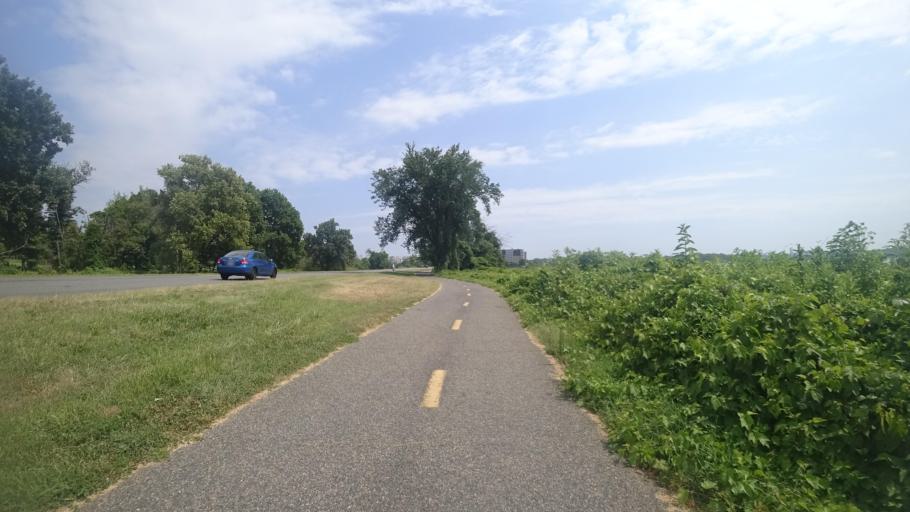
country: US
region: Virginia
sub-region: Fairfax County
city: Belle Haven
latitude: 38.7857
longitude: -77.0540
